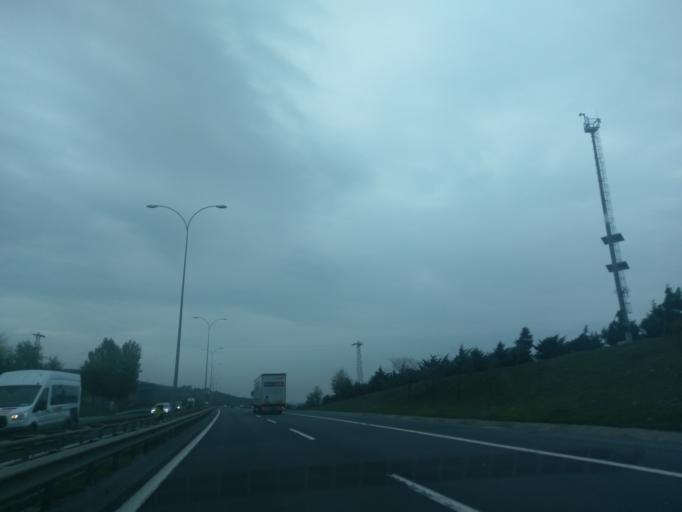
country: TR
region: Istanbul
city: Celaliye
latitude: 41.0574
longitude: 28.4178
